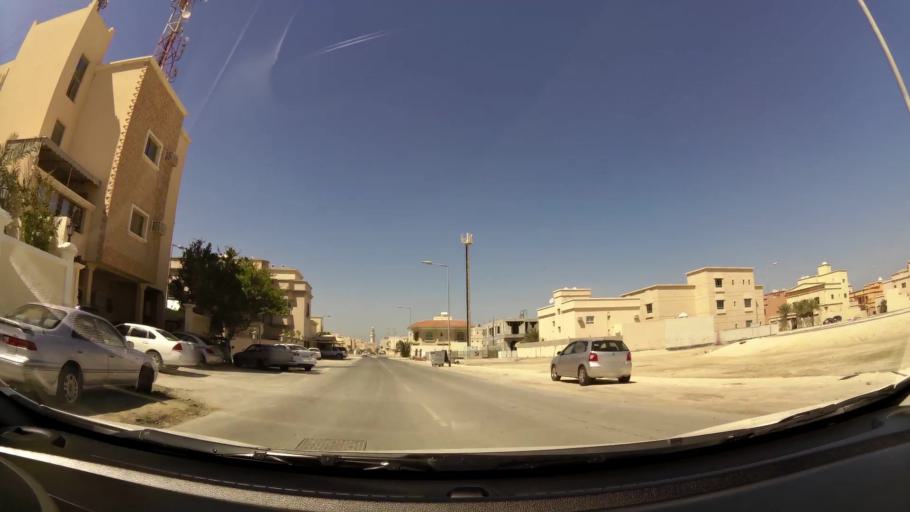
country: BH
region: Muharraq
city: Al Muharraq
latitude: 26.2699
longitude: 50.6016
